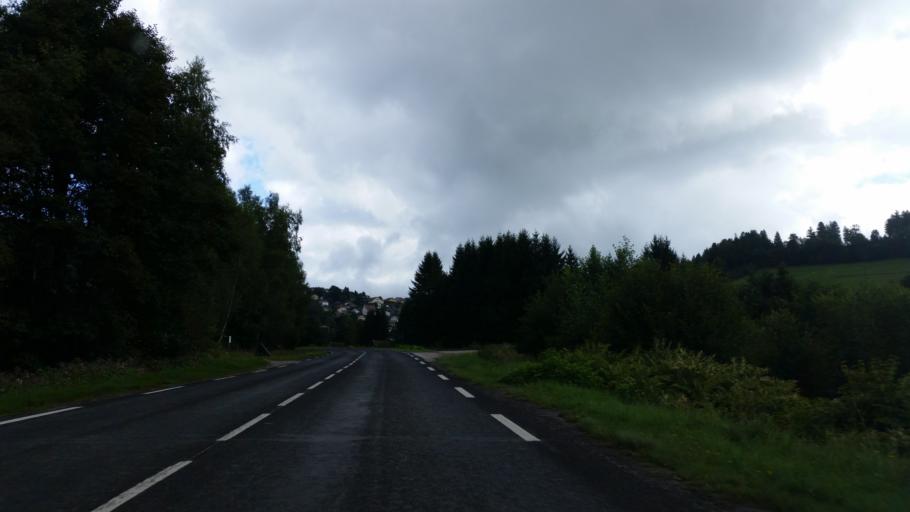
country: FR
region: Lorraine
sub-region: Departement des Vosges
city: Le Tholy
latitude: 48.0747
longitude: 6.7390
